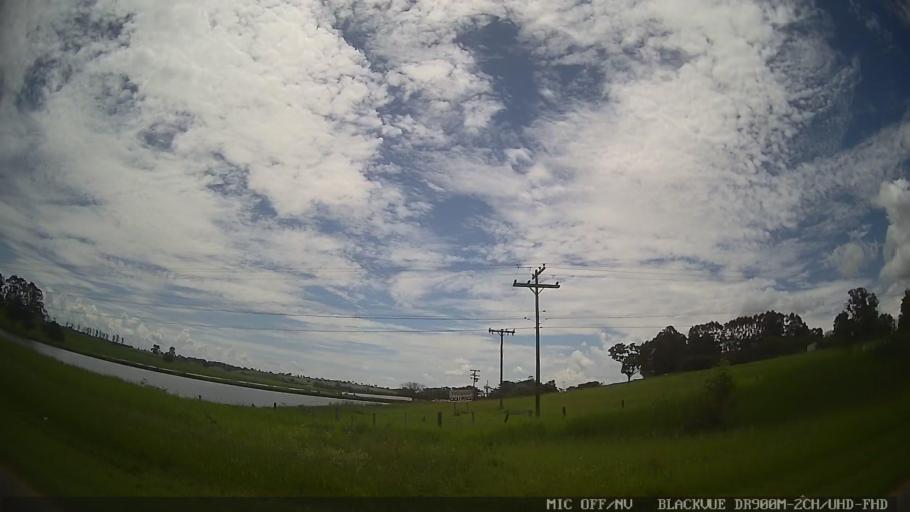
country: BR
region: Sao Paulo
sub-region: Conchas
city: Conchas
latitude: -23.0558
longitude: -47.9613
